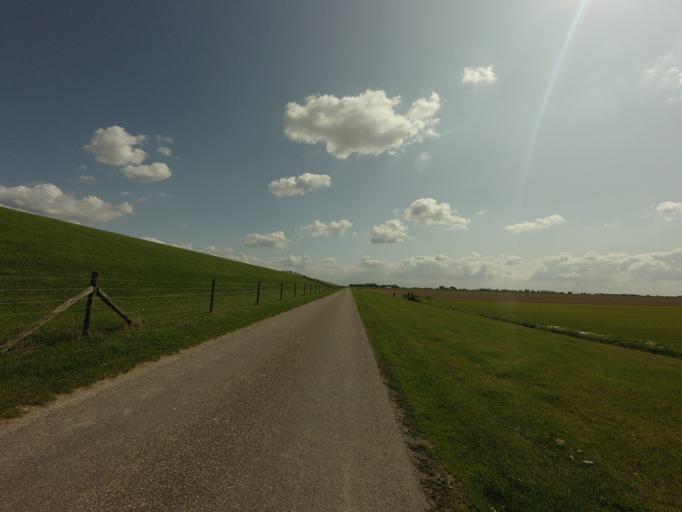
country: NL
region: Friesland
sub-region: Gemeente Ferwerderadiel
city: Hallum
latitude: 53.3213
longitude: 5.7463
